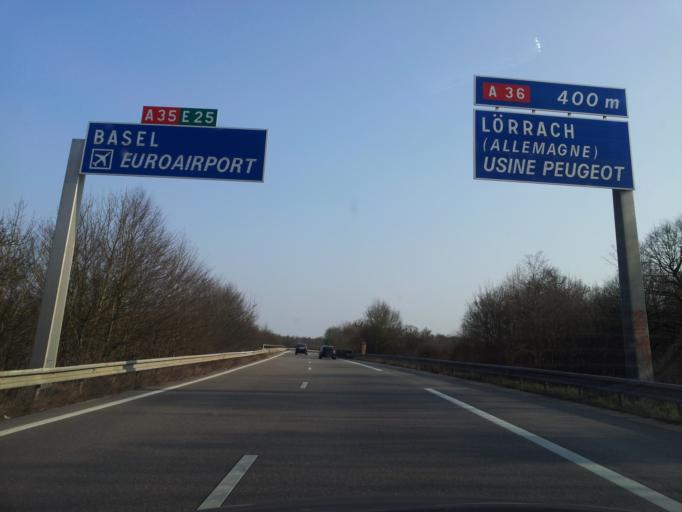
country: FR
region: Alsace
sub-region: Departement du Haut-Rhin
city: Baldersheim
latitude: 47.7847
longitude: 7.4011
